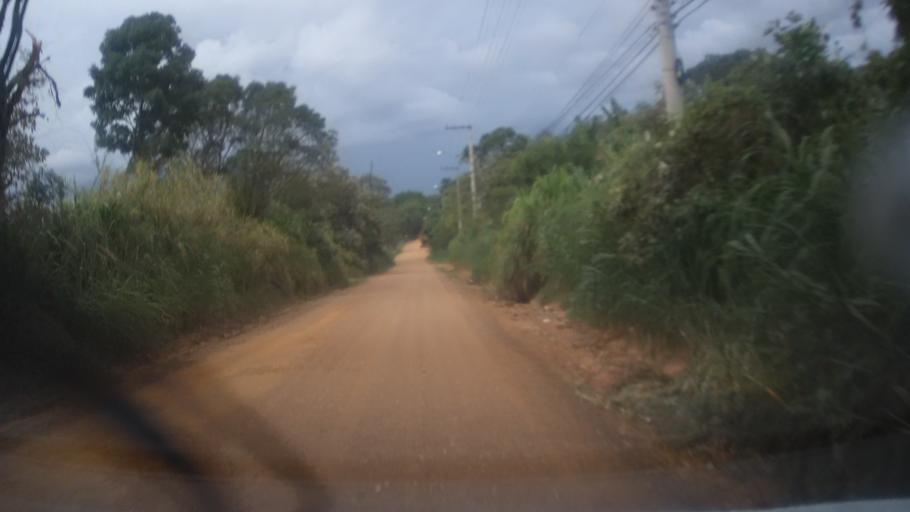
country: BR
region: Sao Paulo
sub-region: Itupeva
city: Itupeva
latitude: -23.1943
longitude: -47.0096
